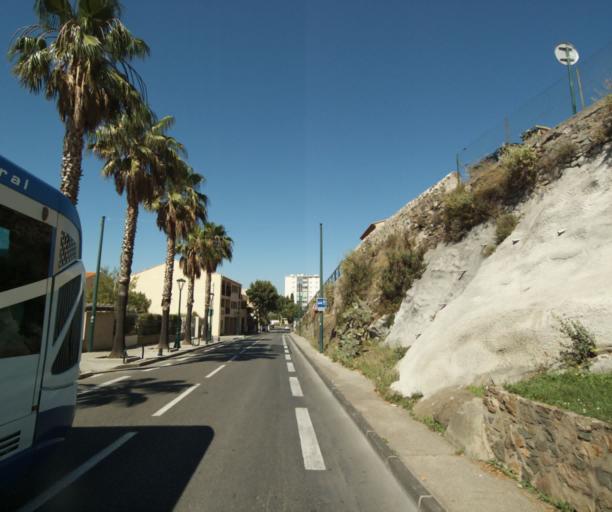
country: FR
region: Provence-Alpes-Cote d'Azur
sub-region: Departement du Var
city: La Garde
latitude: 43.1261
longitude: 6.0121
